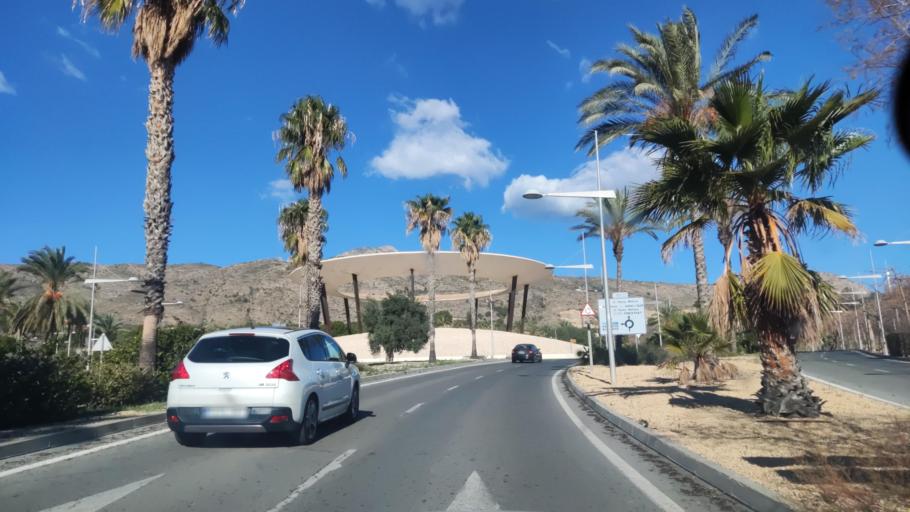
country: ES
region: Valencia
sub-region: Provincia de Alicante
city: Benidorm
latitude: 38.5485
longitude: -0.1629
